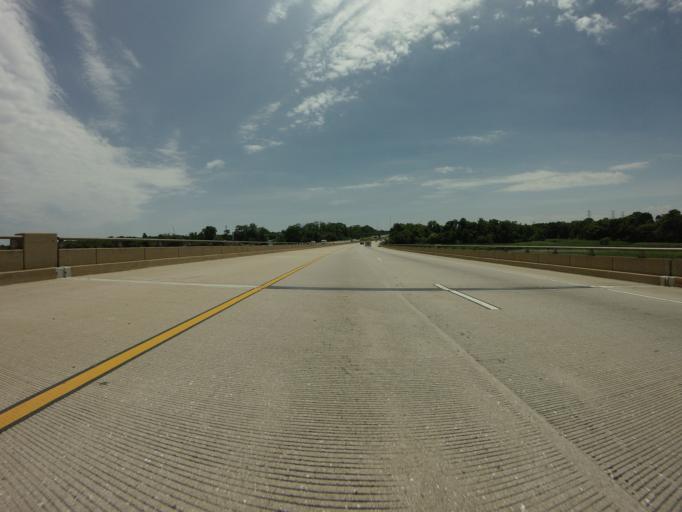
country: US
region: Maryland
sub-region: Baltimore County
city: Rosedale
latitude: 39.3048
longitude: -76.5008
